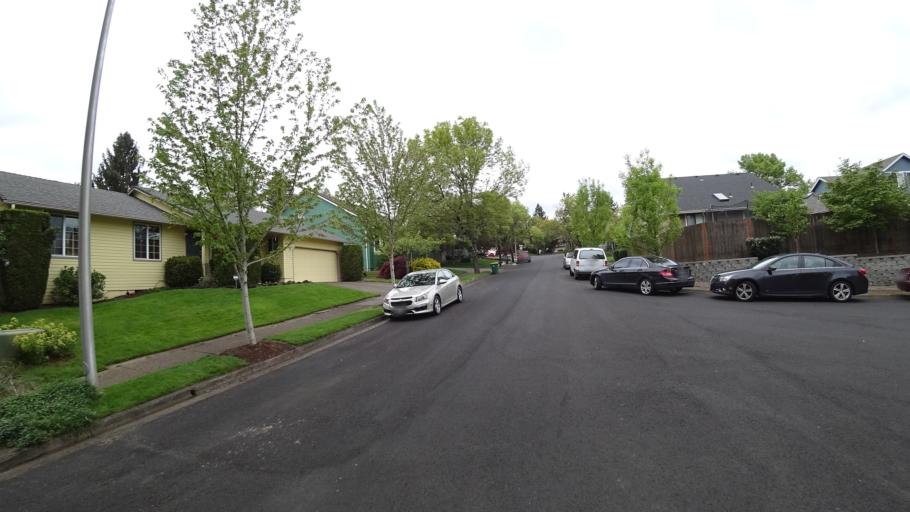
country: US
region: Oregon
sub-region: Washington County
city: Beaverton
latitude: 45.4536
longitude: -122.8231
